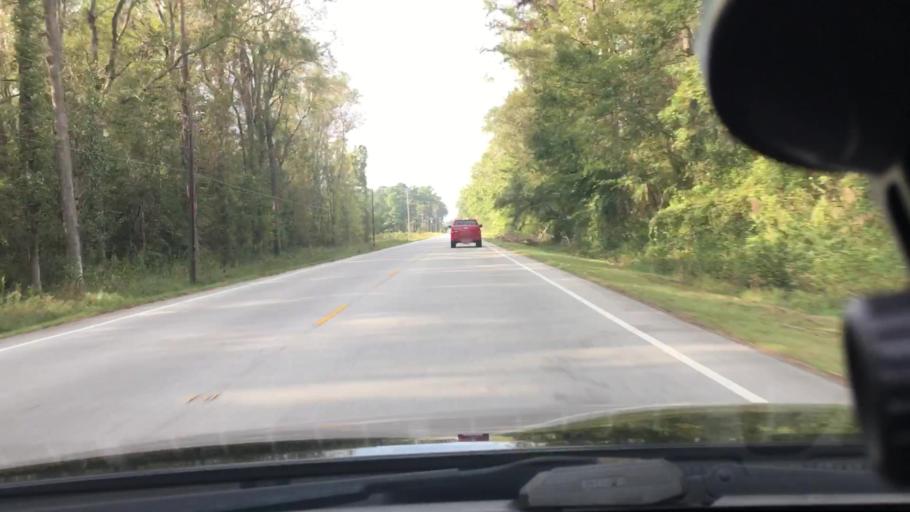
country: US
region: North Carolina
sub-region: Craven County
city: New Bern
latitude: 35.2088
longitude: -77.0605
